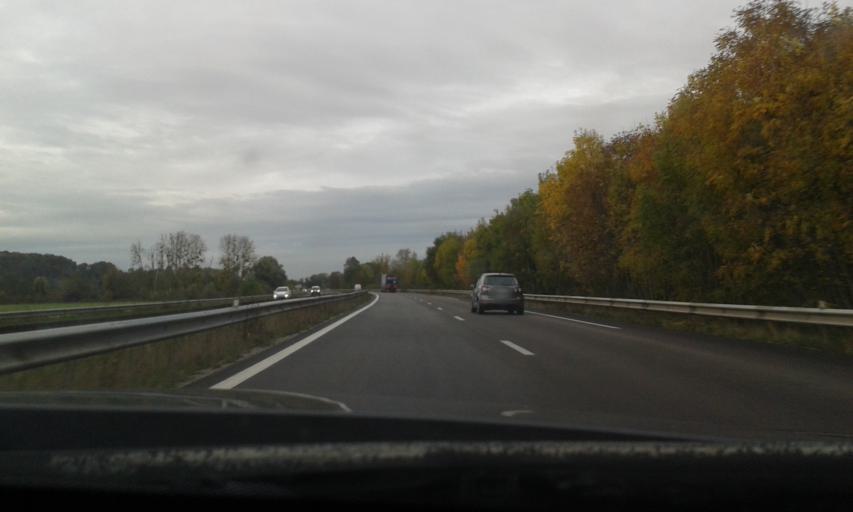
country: FR
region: Haute-Normandie
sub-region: Departement de l'Eure
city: Heudreville-sur-Eure
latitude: 49.1528
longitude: 1.1825
